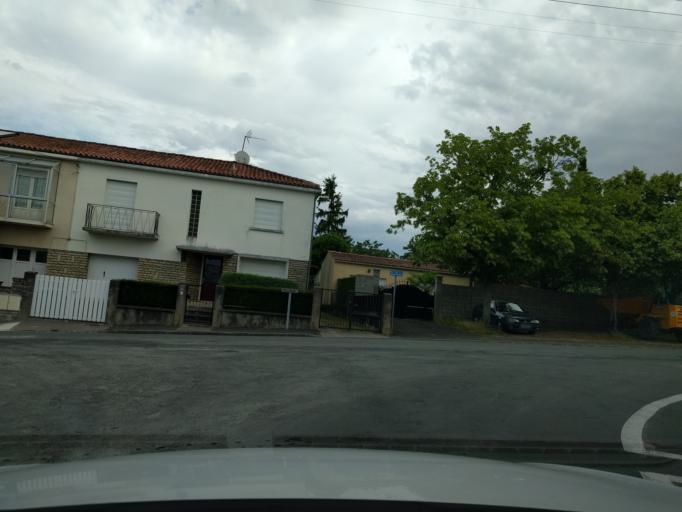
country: FR
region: Poitou-Charentes
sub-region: Departement des Deux-Sevres
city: Niort
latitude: 46.3178
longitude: -0.4394
